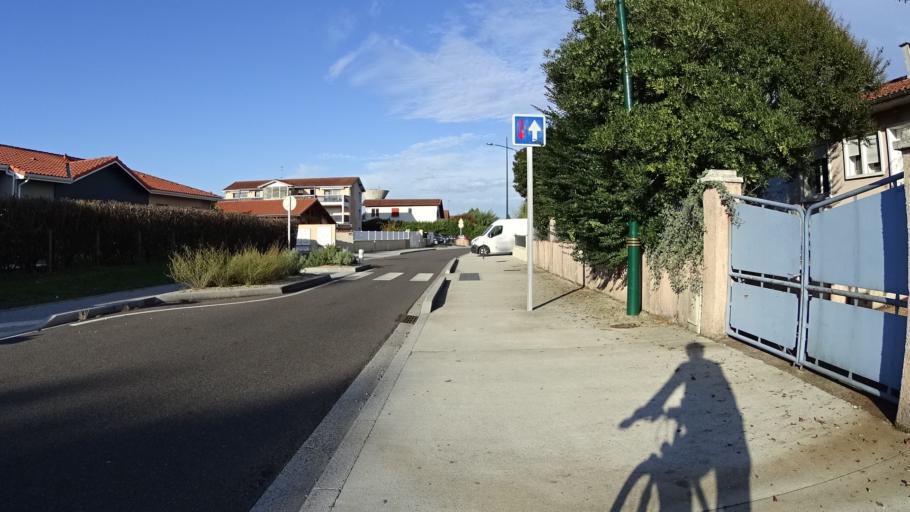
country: FR
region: Aquitaine
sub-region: Departement des Landes
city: Saint-Paul-les-Dax
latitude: 43.7287
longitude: -1.0595
